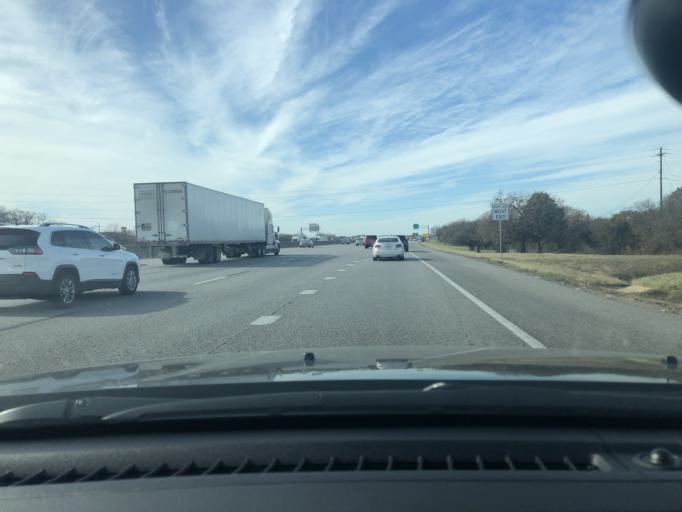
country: US
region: Texas
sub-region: Tarrant County
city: Dalworthington Gardens
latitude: 32.6748
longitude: -97.1428
